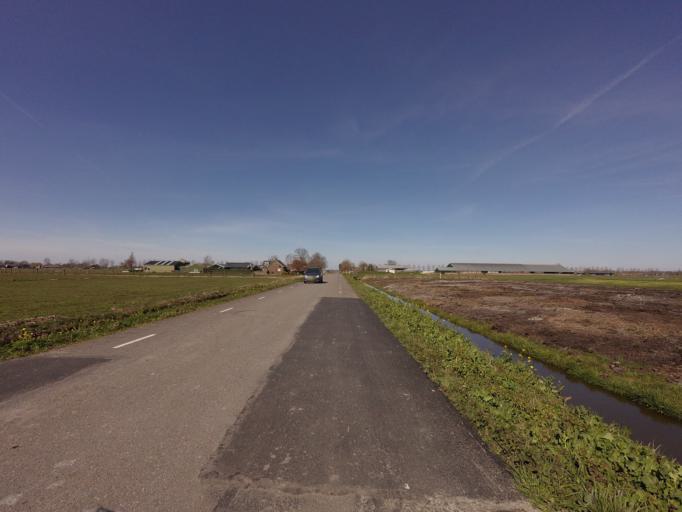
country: NL
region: Utrecht
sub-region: Gemeente De Ronde Venen
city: Mijdrecht
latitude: 52.1896
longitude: 4.8504
